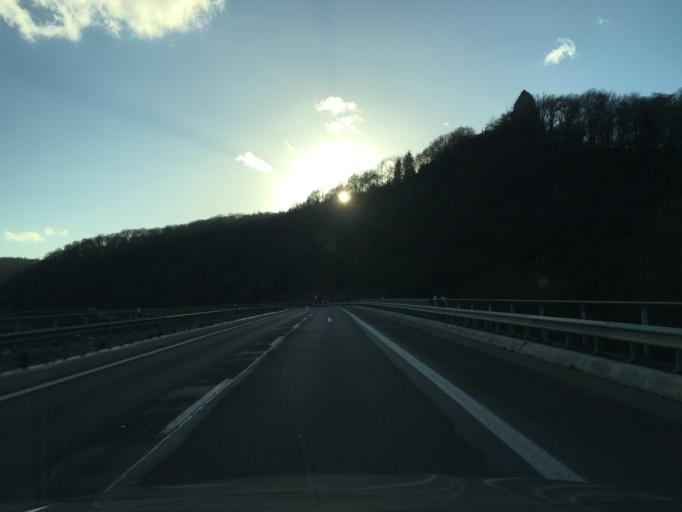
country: DE
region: Rheinland-Pfalz
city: Unkel
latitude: 50.5984
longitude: 7.2085
